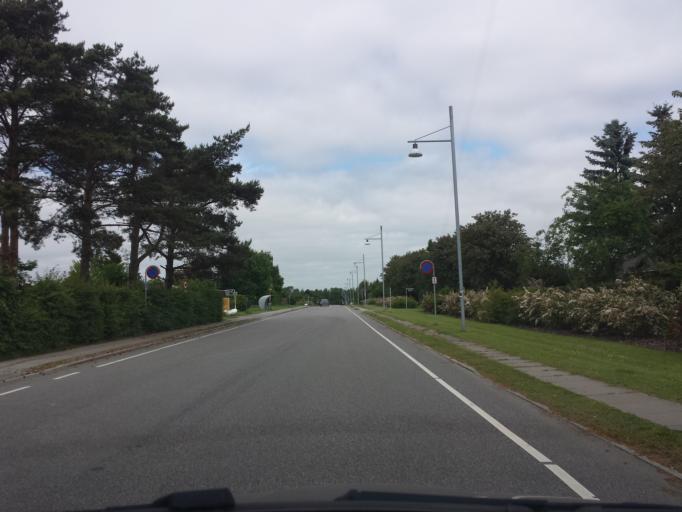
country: DK
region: Capital Region
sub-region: Glostrup Kommune
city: Glostrup
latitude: 55.7007
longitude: 12.4035
